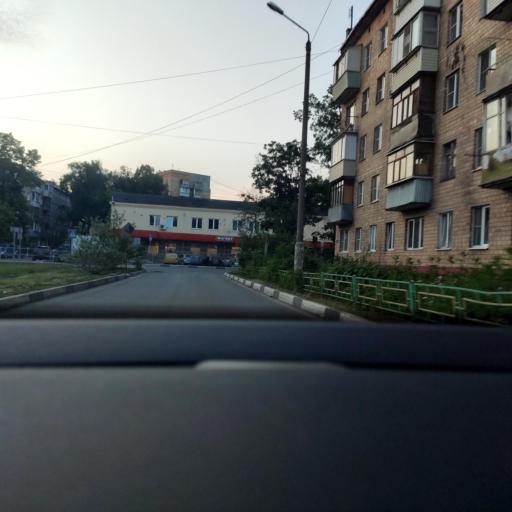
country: RU
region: Moskovskaya
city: Zheleznodorozhnyy
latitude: 55.7474
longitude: 37.9763
